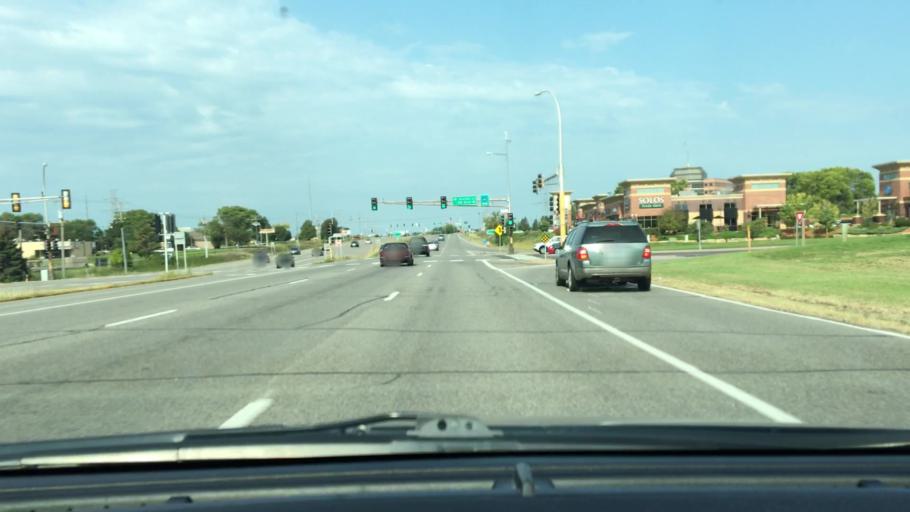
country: US
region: Minnesota
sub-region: Hennepin County
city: Plymouth
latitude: 45.0081
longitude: -93.4500
